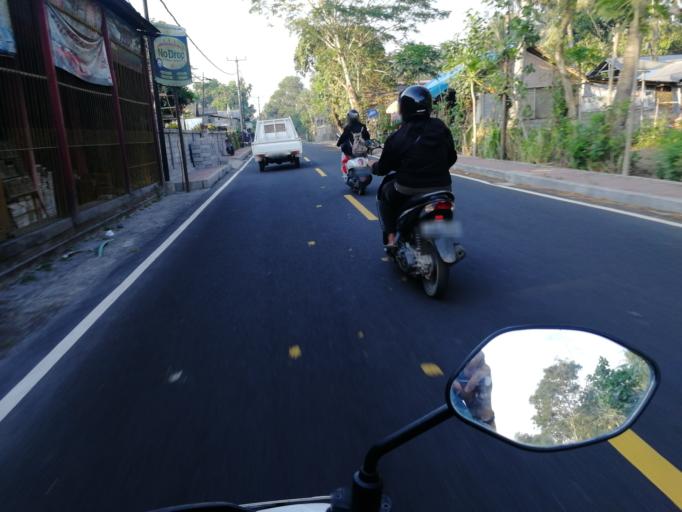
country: ID
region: Bali
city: Tistagede
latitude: -8.3804
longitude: 115.6085
